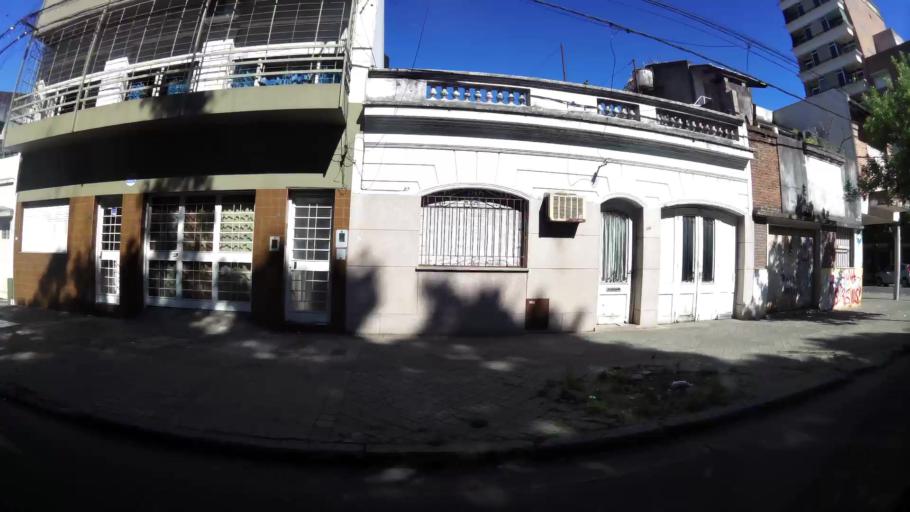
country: AR
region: Santa Fe
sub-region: Departamento de Rosario
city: Rosario
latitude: -32.9469
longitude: -60.6740
